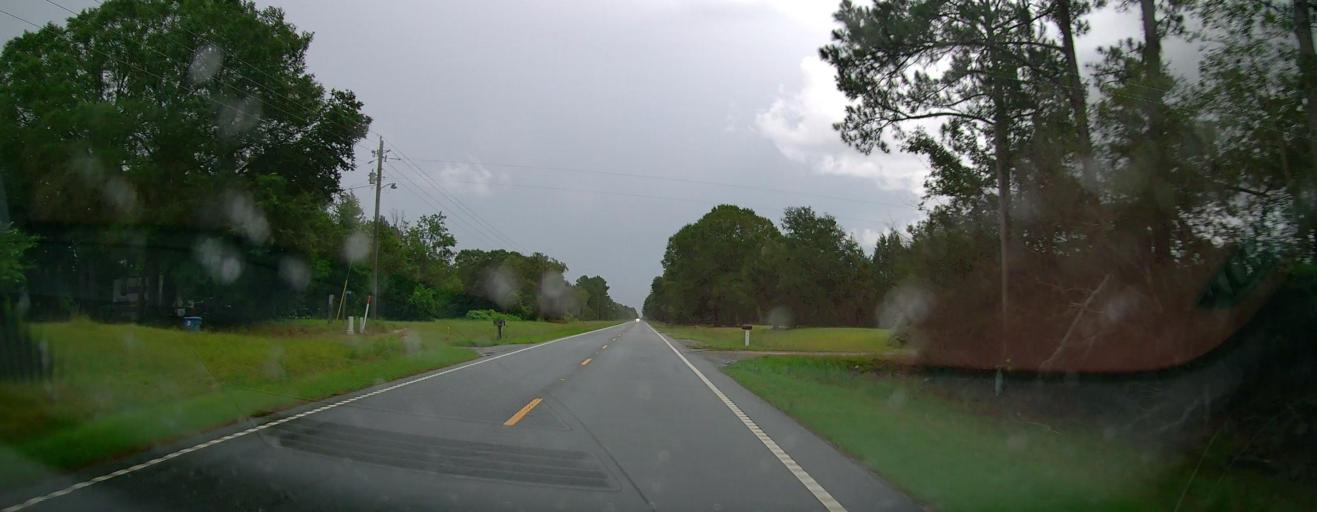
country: US
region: Georgia
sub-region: Brantley County
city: Nahunta
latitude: 31.3431
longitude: -81.9925
